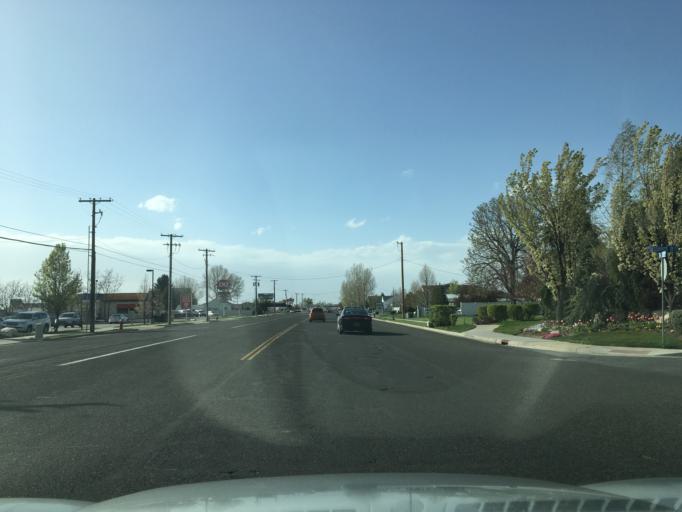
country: US
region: Utah
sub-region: Davis County
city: Kaysville
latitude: 41.0475
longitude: -111.9546
